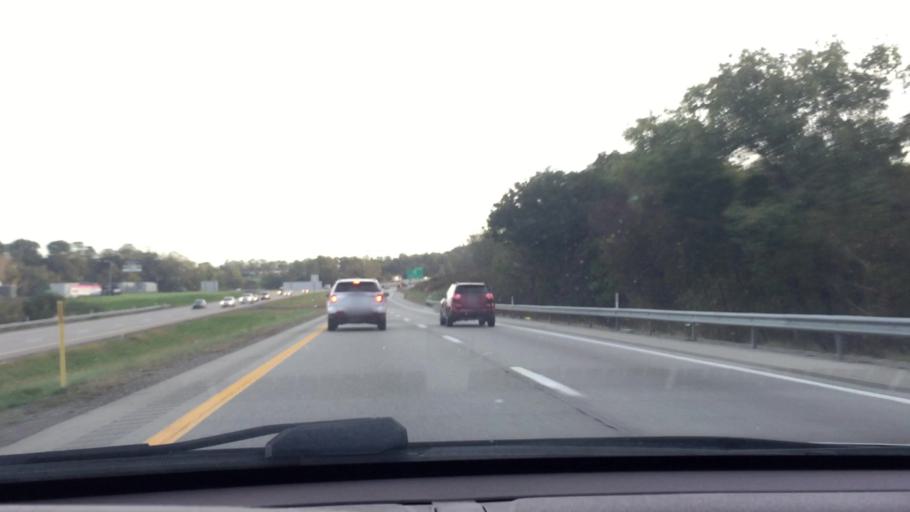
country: US
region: Pennsylvania
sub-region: Washington County
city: Houston
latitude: 40.2394
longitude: -80.2062
